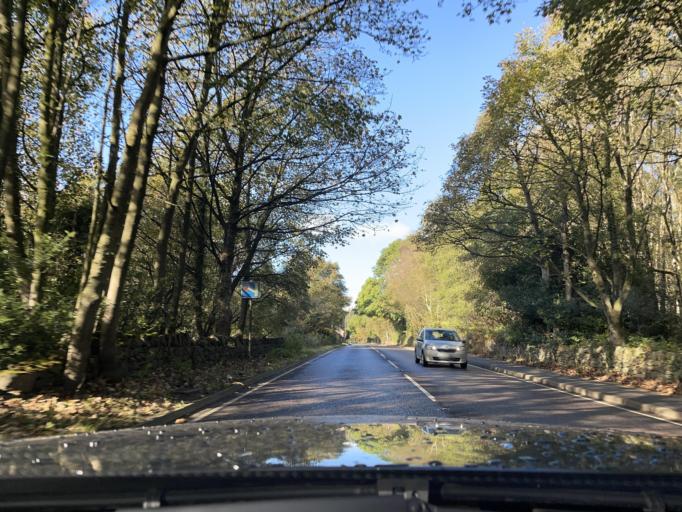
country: GB
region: England
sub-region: Sheffield
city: Bradfield
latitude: 53.3784
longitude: -1.5840
